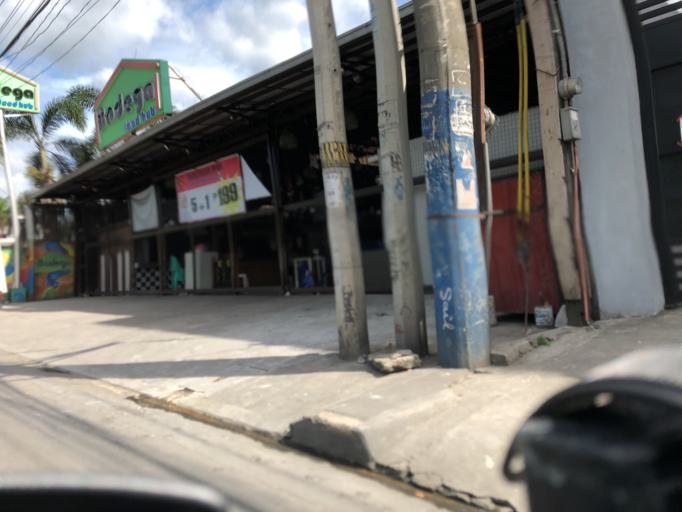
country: PH
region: Calabarzon
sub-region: Province of Rizal
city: San Mateo
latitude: 14.7285
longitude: 121.0599
